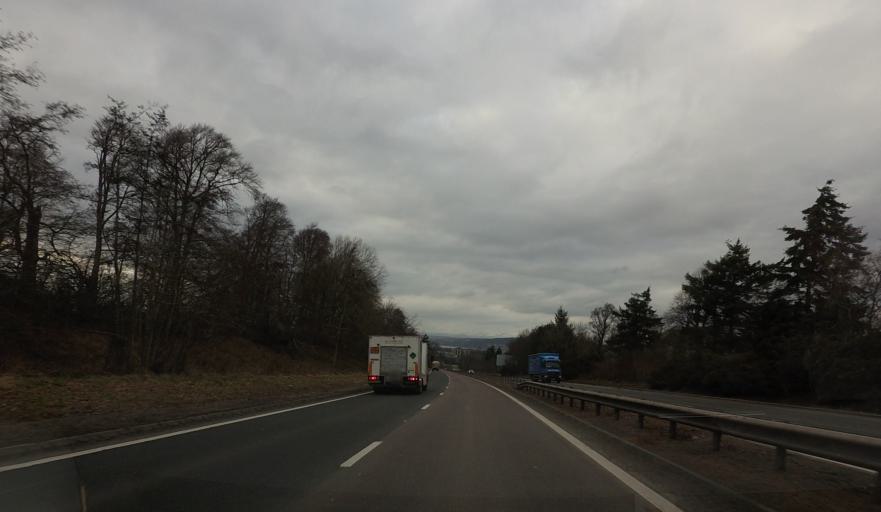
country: GB
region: Scotland
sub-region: Highland
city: Inverness
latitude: 57.4637
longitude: -4.1714
